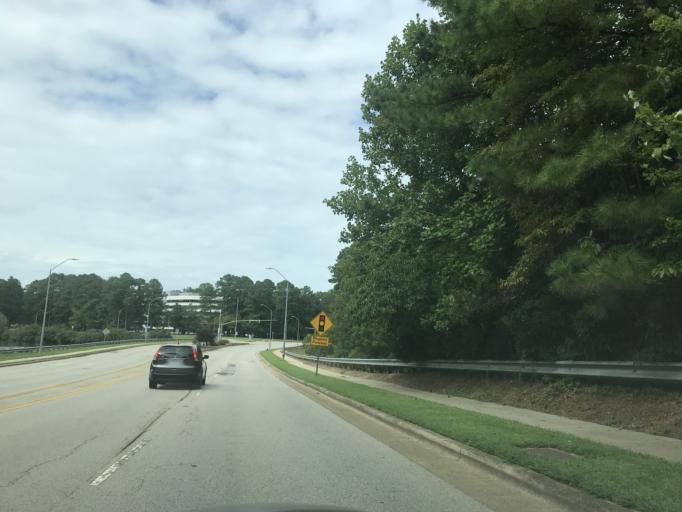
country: US
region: North Carolina
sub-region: Wake County
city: Apex
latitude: 35.7264
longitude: -78.7924
